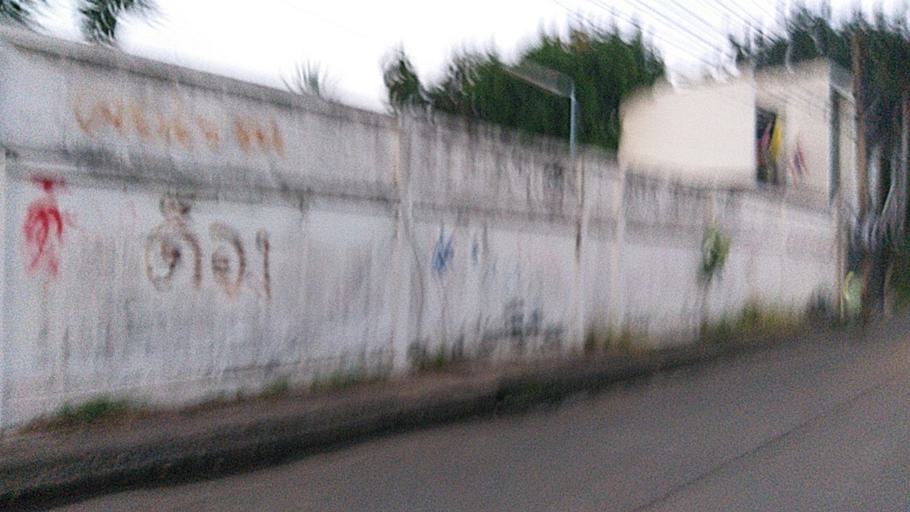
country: TH
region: Bangkok
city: Lat Phrao
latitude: 13.8258
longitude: 100.6101
